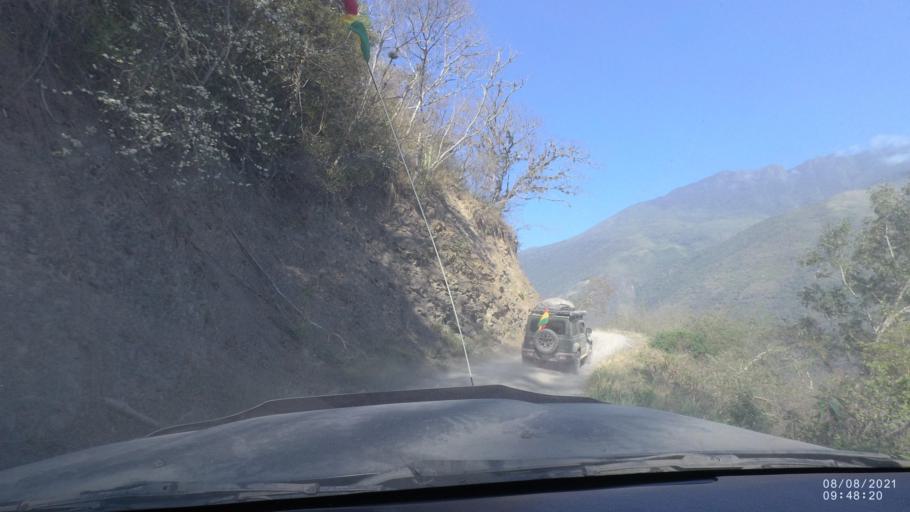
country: BO
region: La Paz
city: Quime
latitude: -16.6125
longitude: -66.7287
